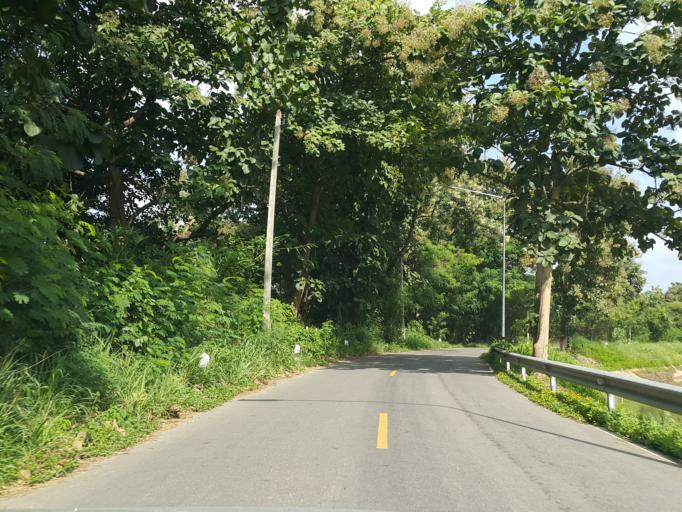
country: TH
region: Chiang Mai
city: San Sai
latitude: 18.9080
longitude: 99.0127
